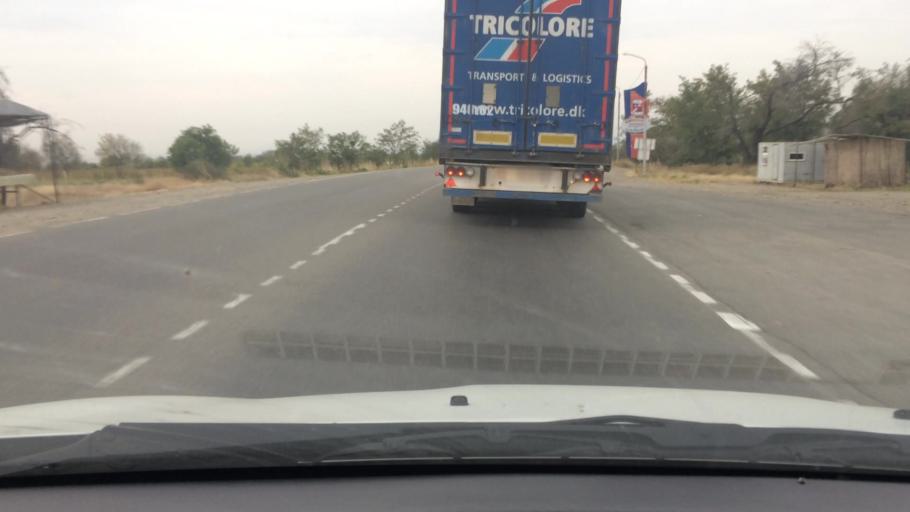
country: GE
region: T'bilisi
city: Tbilisi
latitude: 41.5914
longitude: 44.7803
